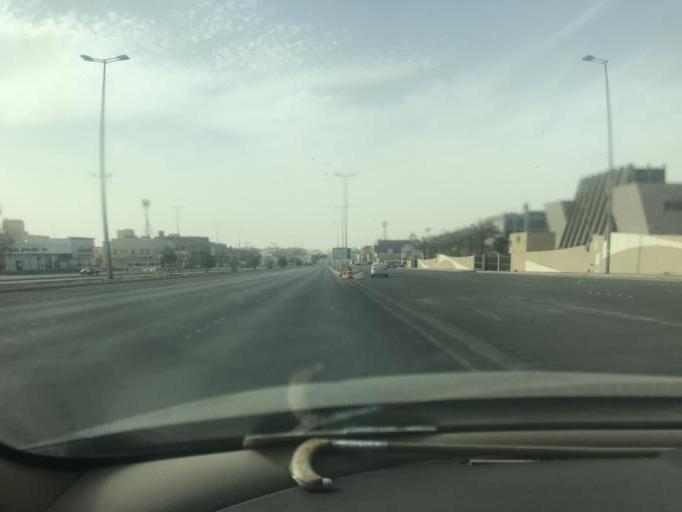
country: SA
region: Ar Riyad
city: Riyadh
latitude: 24.8253
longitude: 46.6842
